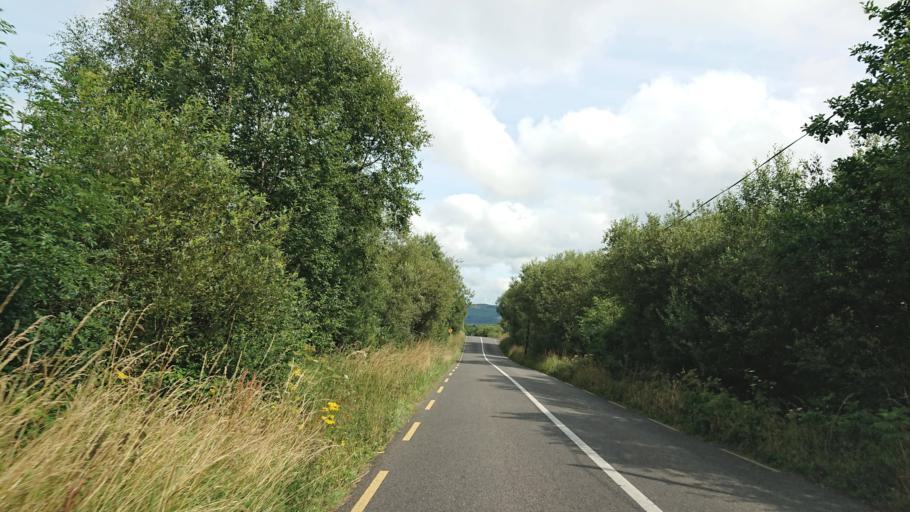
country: IE
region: Connaught
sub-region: County Leitrim
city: Carrick-on-Shannon
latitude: 54.0246
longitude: -8.1702
